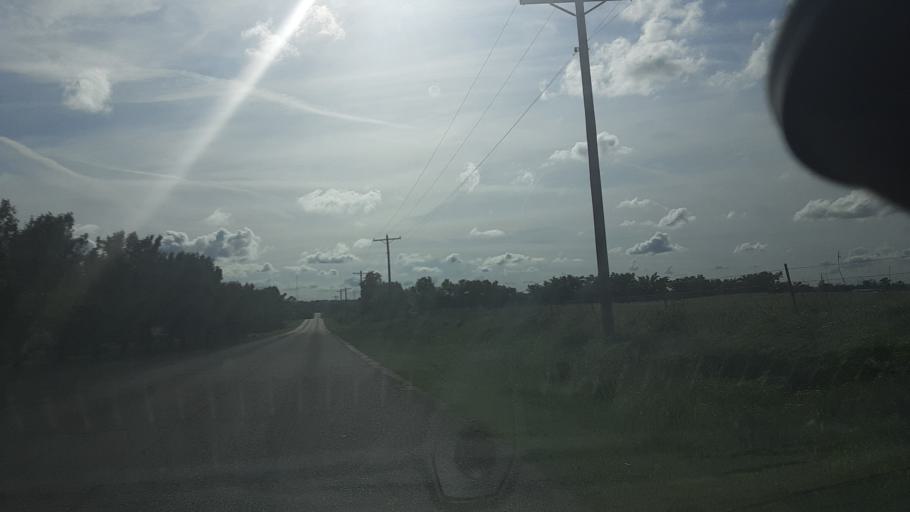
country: US
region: Oklahoma
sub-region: Logan County
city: Langston
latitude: 36.0577
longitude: -97.3965
